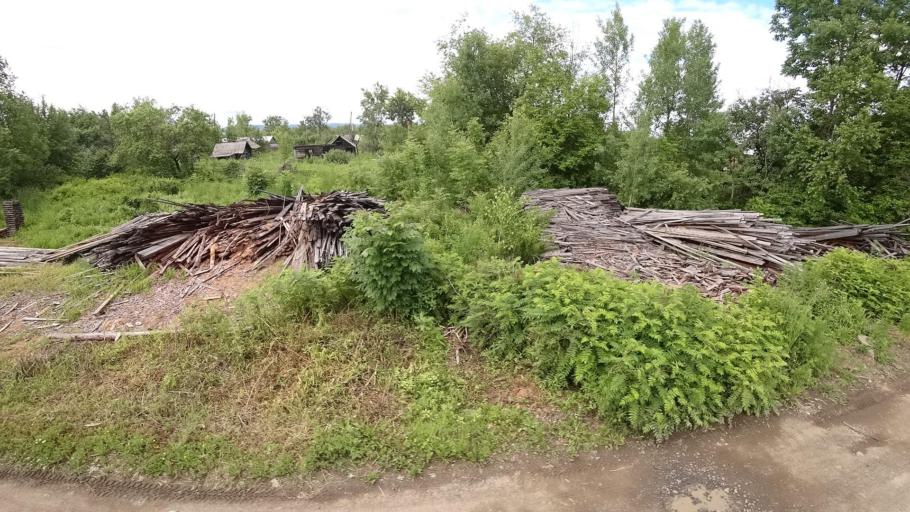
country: RU
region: Khabarovsk Krai
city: Litovko
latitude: 49.3673
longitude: 135.1724
